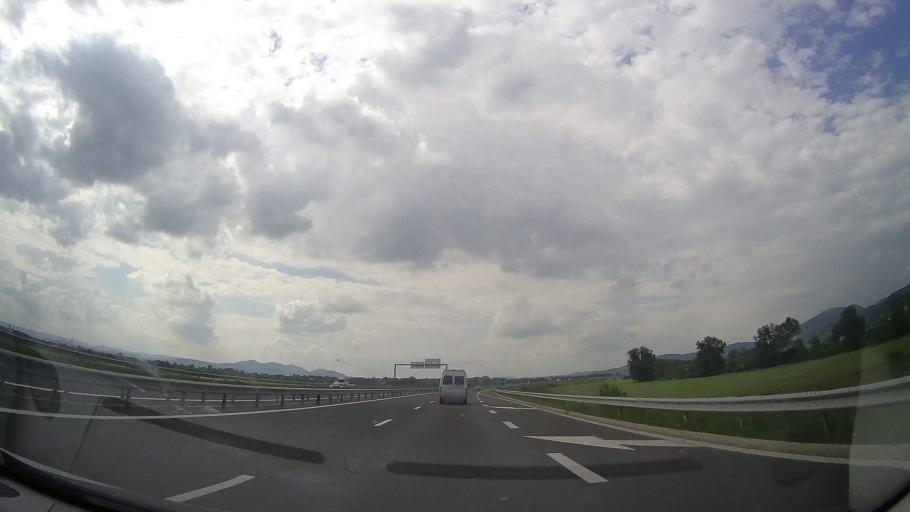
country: RO
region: Hunedoara
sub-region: Oras Simeria
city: Simeria
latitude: 45.8523
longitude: 23.0374
